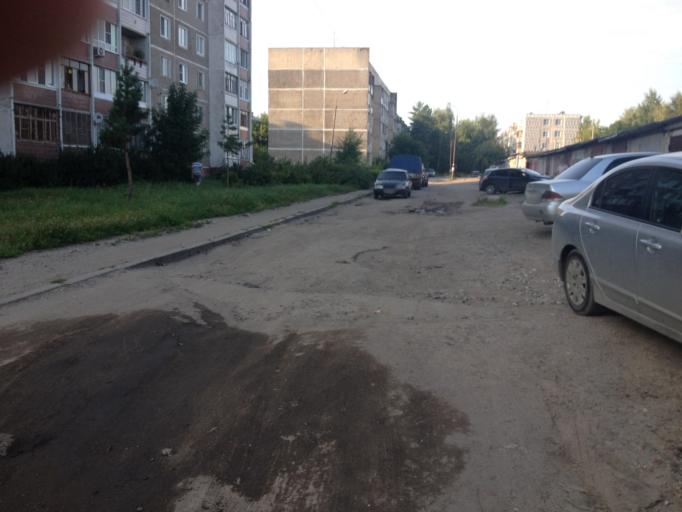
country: RU
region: Ivanovo
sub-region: Gorod Ivanovo
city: Ivanovo
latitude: 56.9575
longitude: 40.9972
